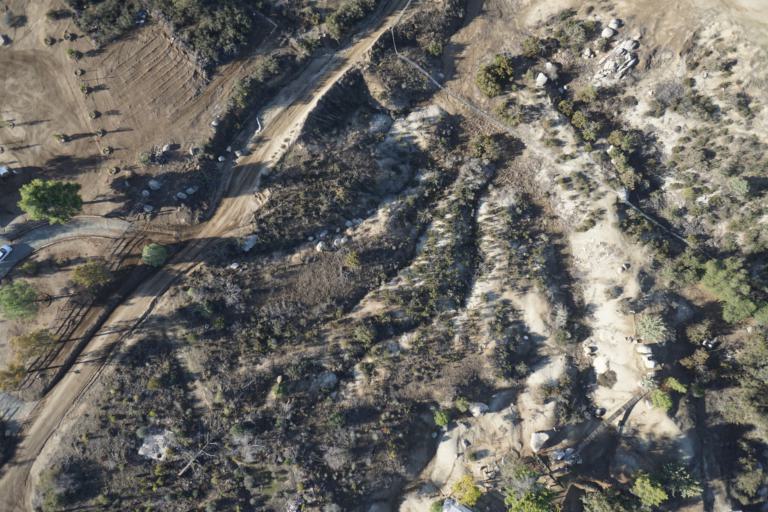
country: US
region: California
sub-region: Riverside County
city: Valle Vista
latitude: 33.6278
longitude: -116.8911
